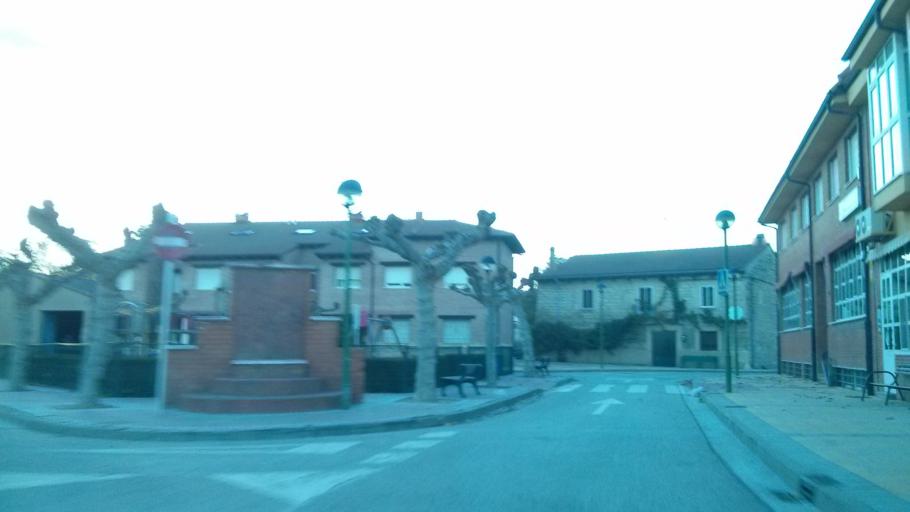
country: ES
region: Castille and Leon
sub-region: Provincia de Burgos
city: Villalbilla de Burgos
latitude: 42.3608
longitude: -3.7733
